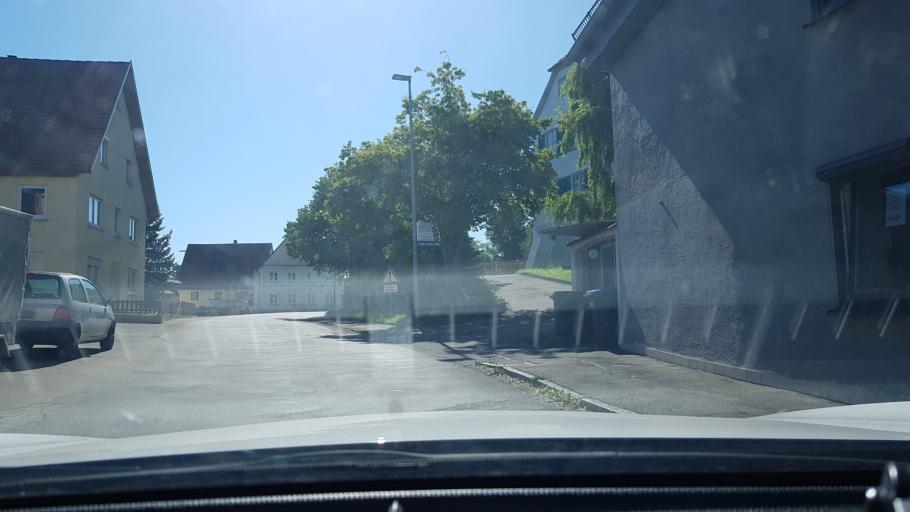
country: DE
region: Baden-Wuerttemberg
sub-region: Tuebingen Region
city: Gutenzell-Hurbel
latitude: 48.1095
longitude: 9.9470
